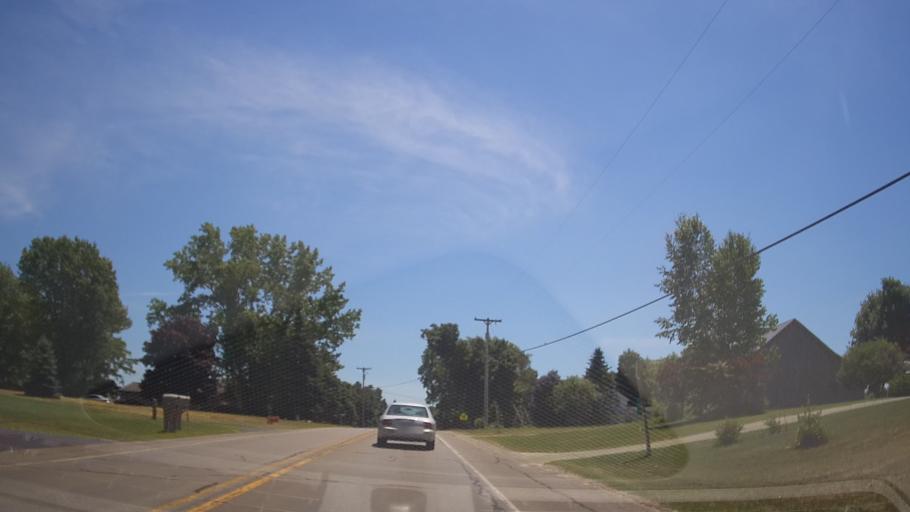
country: US
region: Michigan
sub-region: Grand Traverse County
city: Traverse City
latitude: 44.6966
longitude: -85.6919
